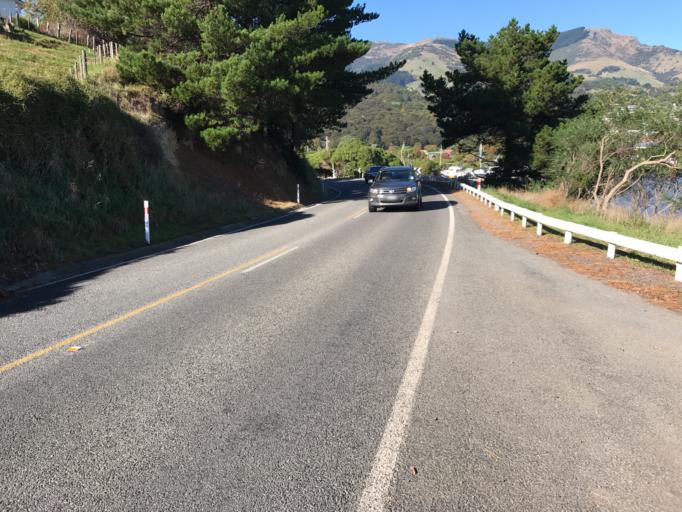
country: NZ
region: Canterbury
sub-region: Christchurch City
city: Christchurch
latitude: -43.7991
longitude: 172.9673
